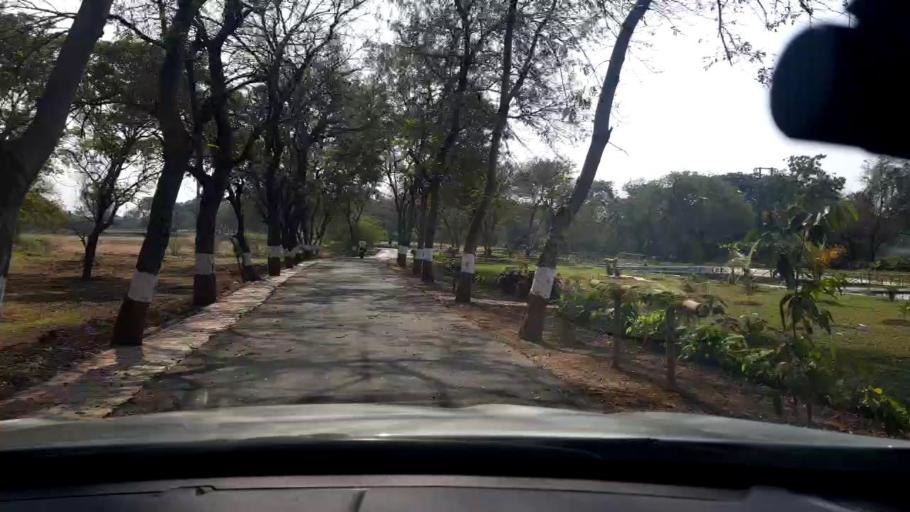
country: IN
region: Maharashtra
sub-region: Pune Division
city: Shivaji Nagar
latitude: 18.5434
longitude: 73.8559
